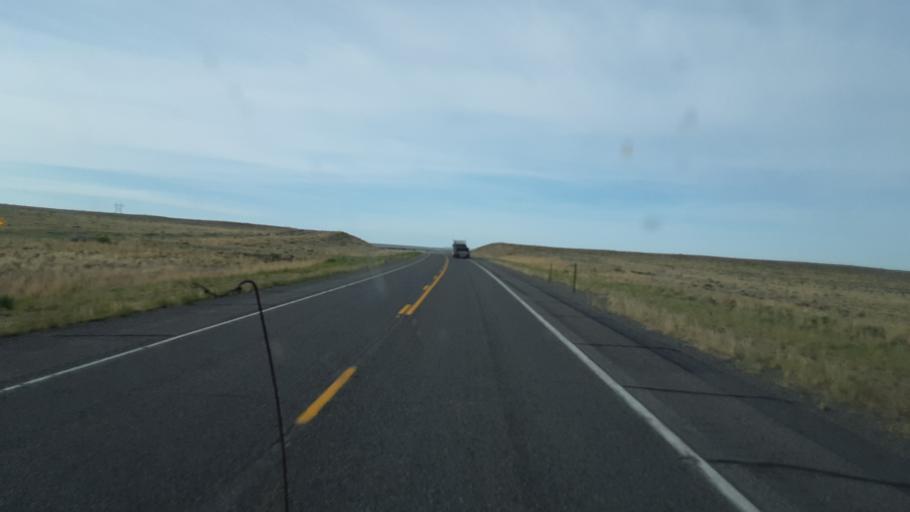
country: US
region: Wyoming
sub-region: Hot Springs County
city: Thermopolis
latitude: 43.2931
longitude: -108.1287
